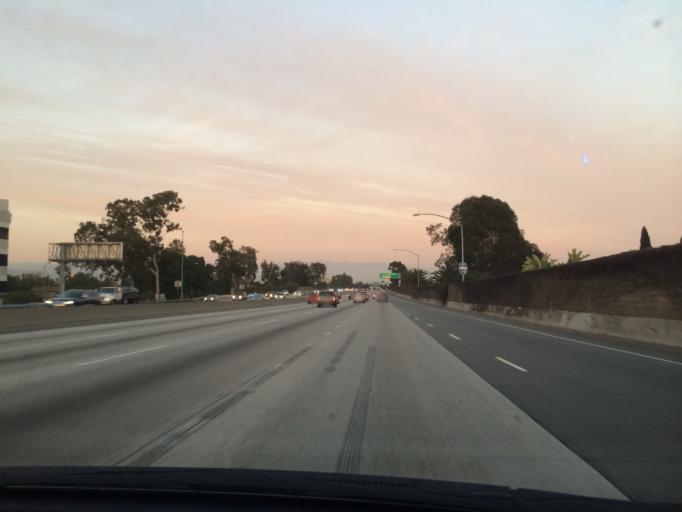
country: US
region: California
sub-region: Los Angeles County
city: Culver City
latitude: 34.0315
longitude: -118.3896
